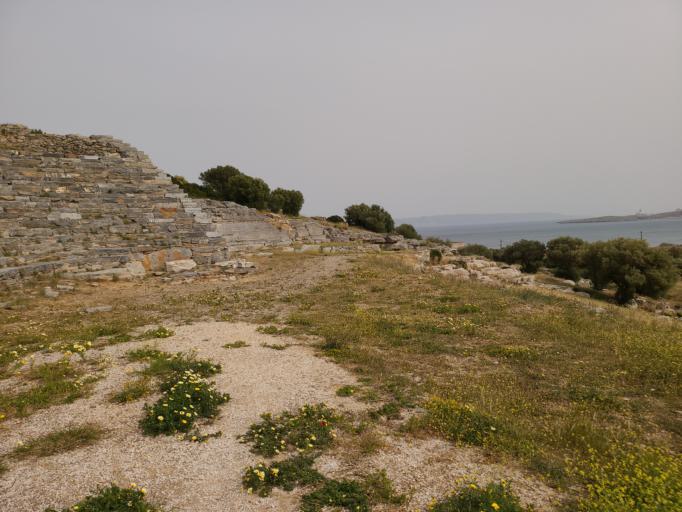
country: GR
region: Attica
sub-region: Nomarchia Anatolikis Attikis
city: Lavrio
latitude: 37.7380
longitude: 24.0536
